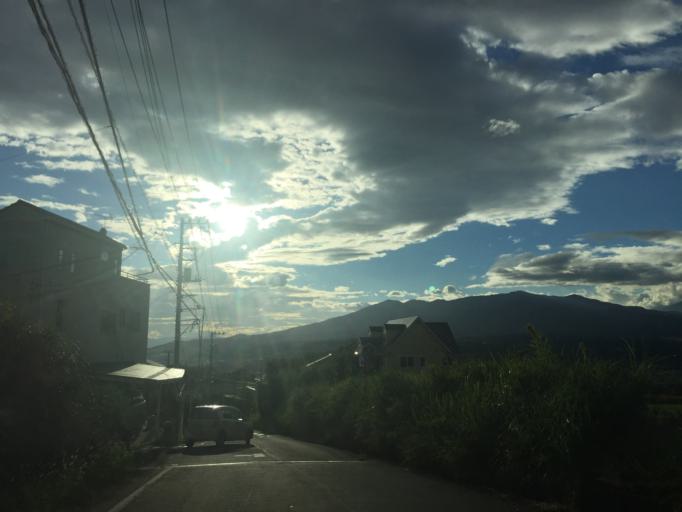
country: JP
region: Shizuoka
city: Mishima
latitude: 35.1585
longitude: 138.9228
